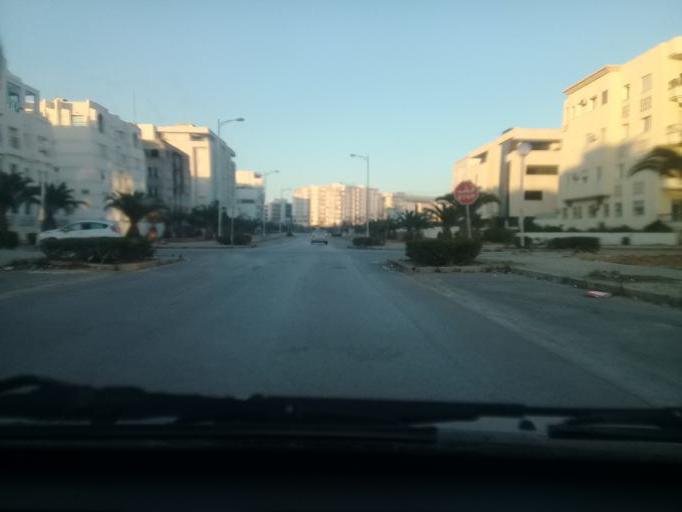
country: TN
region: Tunis
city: La Goulette
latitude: 36.8458
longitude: 10.2746
